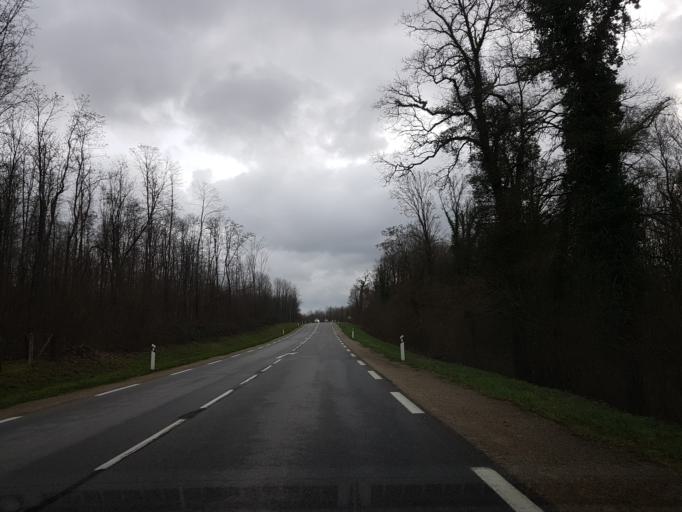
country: FR
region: Champagne-Ardenne
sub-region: Departement de la Haute-Marne
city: Fayl-Billot
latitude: 47.7994
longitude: 5.5621
